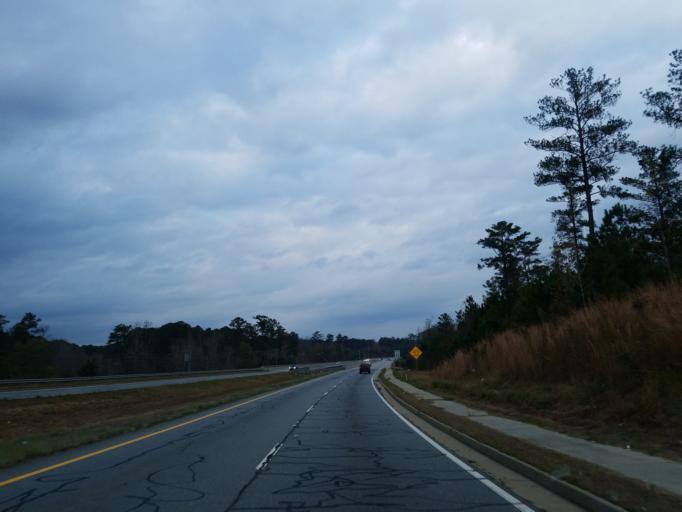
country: US
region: Georgia
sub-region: Cobb County
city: Acworth
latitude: 34.0875
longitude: -84.6542
